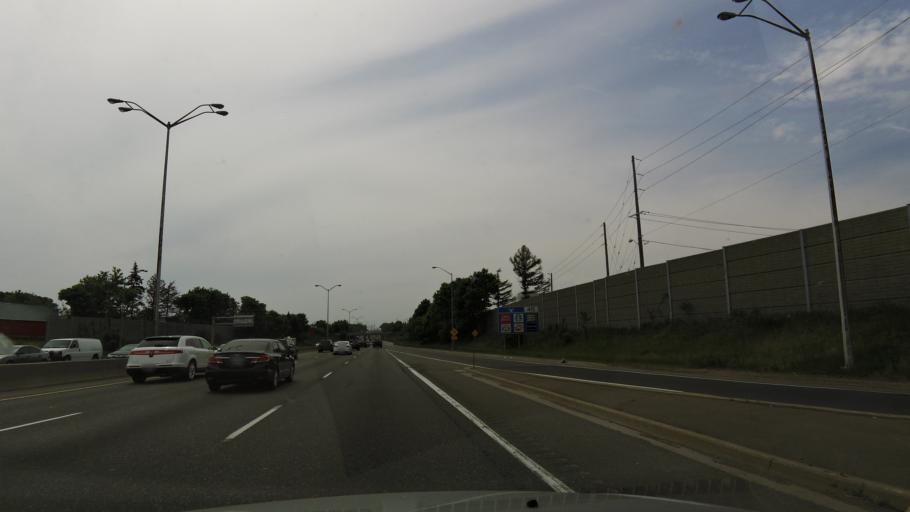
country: CA
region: Ontario
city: Oshawa
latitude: 43.8832
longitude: -78.8491
